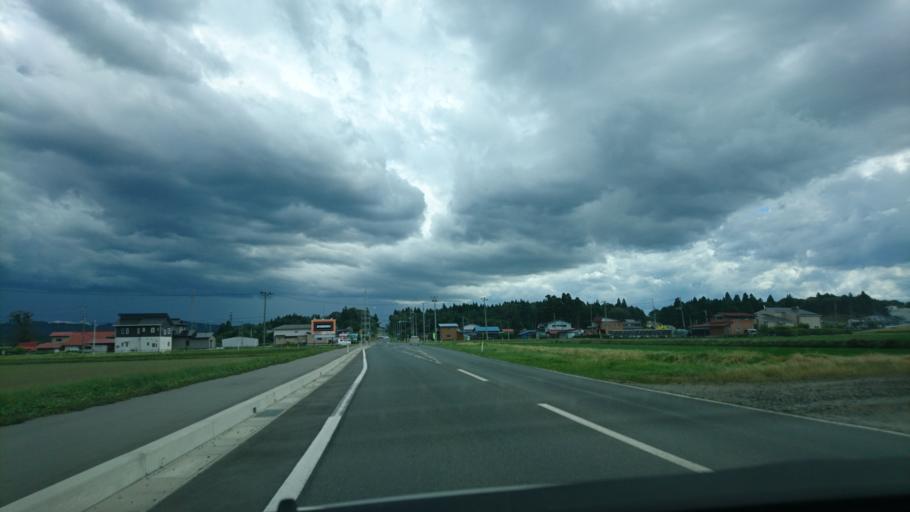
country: JP
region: Iwate
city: Kitakami
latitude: 39.3145
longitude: 141.1268
